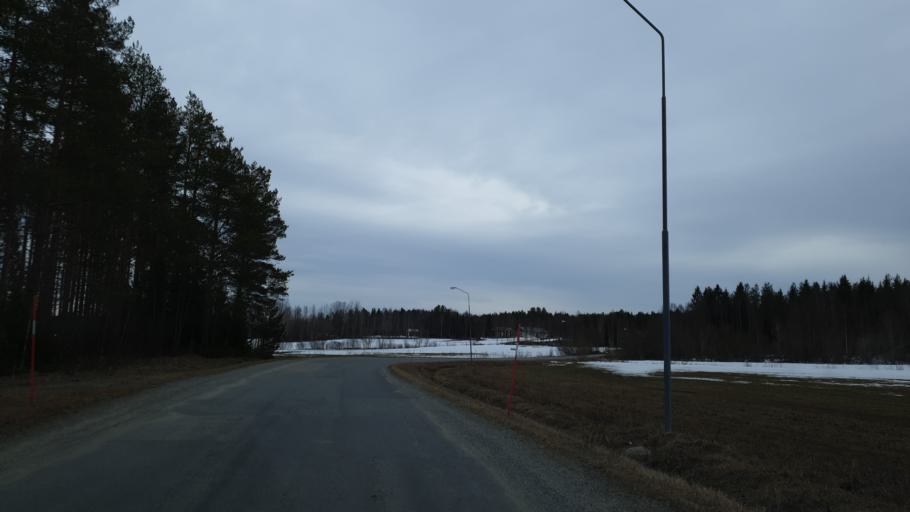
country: SE
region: Vaesterbotten
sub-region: Robertsfors Kommun
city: Robertsfors
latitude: 64.3986
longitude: 21.0031
